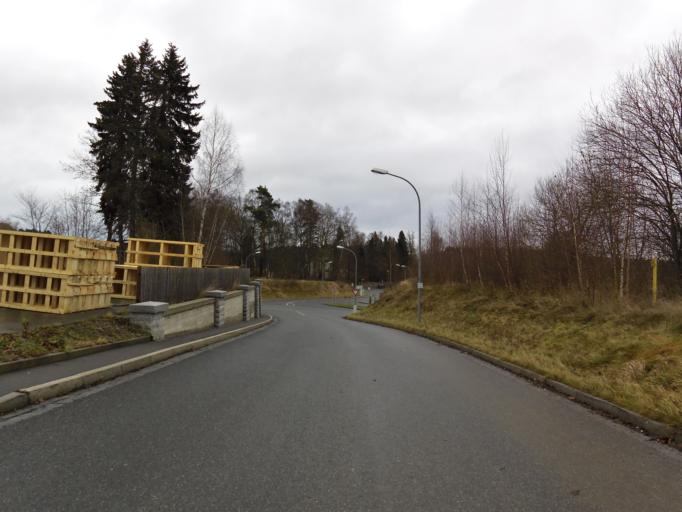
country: DE
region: Bavaria
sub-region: Upper Franconia
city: Wunsiedel
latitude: 50.0489
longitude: 12.0365
